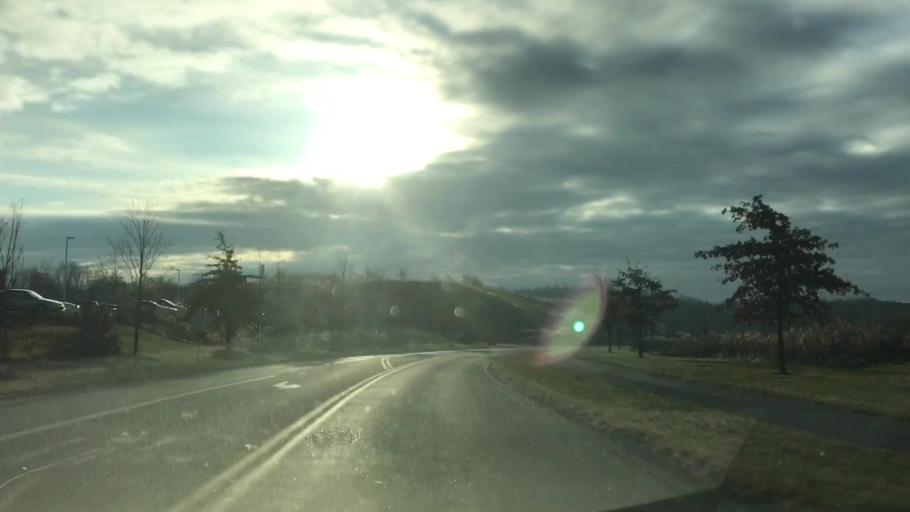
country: US
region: Pennsylvania
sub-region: Allegheny County
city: Carnot-Moon
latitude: 40.4901
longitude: -80.1972
